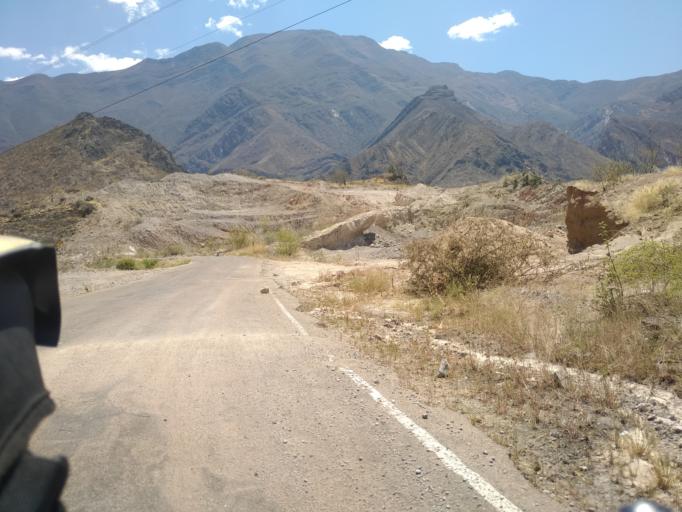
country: PE
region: Amazonas
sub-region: Provincia de Chachapoyas
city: Balsas
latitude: -6.8477
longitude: -78.0398
